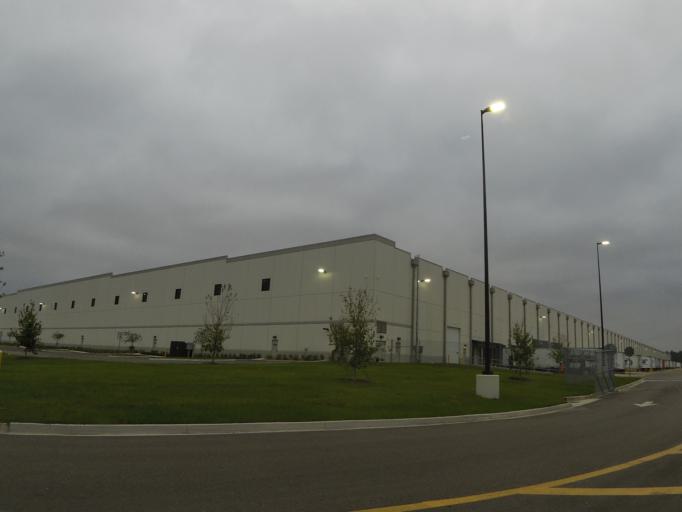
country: US
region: Florida
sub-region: Duval County
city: Baldwin
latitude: 30.2482
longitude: -81.8623
